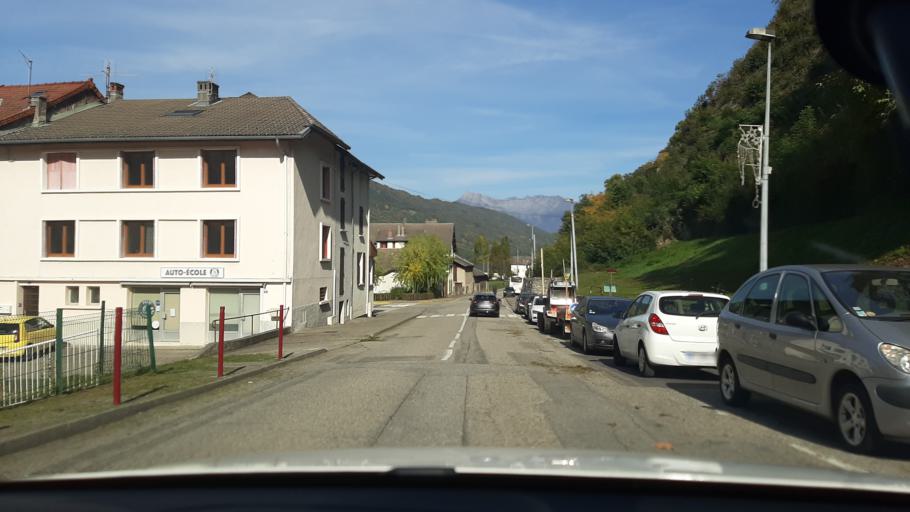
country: FR
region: Rhone-Alpes
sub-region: Departement de la Savoie
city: La Rochette
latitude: 45.4576
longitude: 6.1202
